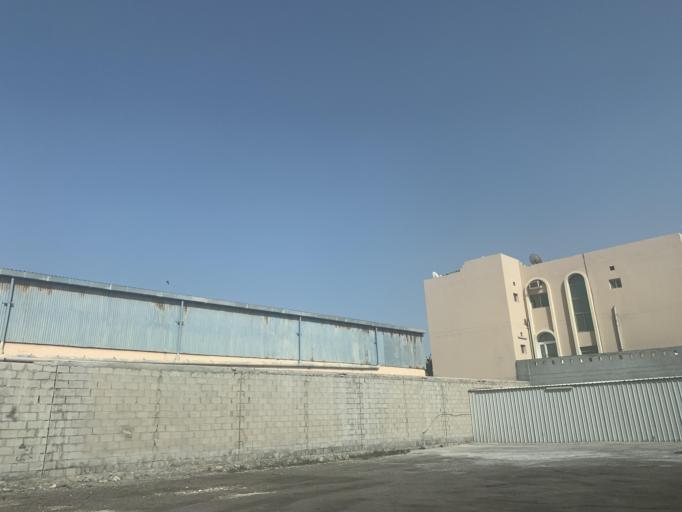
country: BH
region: Northern
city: Sitrah
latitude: 26.1640
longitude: 50.6191
